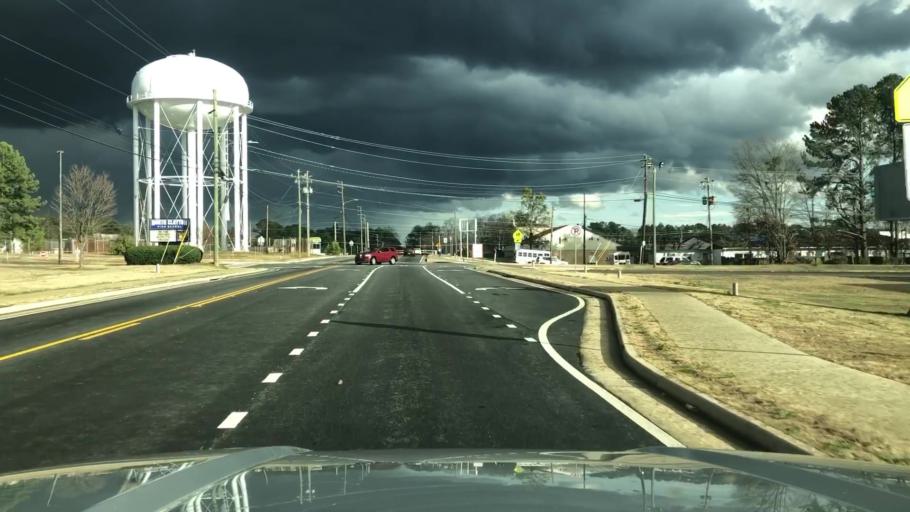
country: US
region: Georgia
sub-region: Clayton County
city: Riverdale
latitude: 33.6081
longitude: -84.4394
